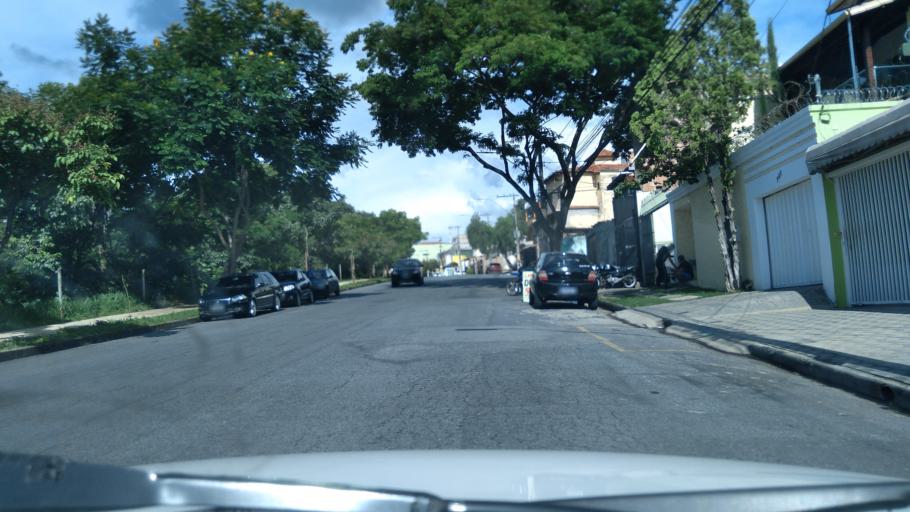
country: BR
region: Minas Gerais
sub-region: Belo Horizonte
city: Belo Horizonte
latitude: -19.8611
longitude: -43.8867
